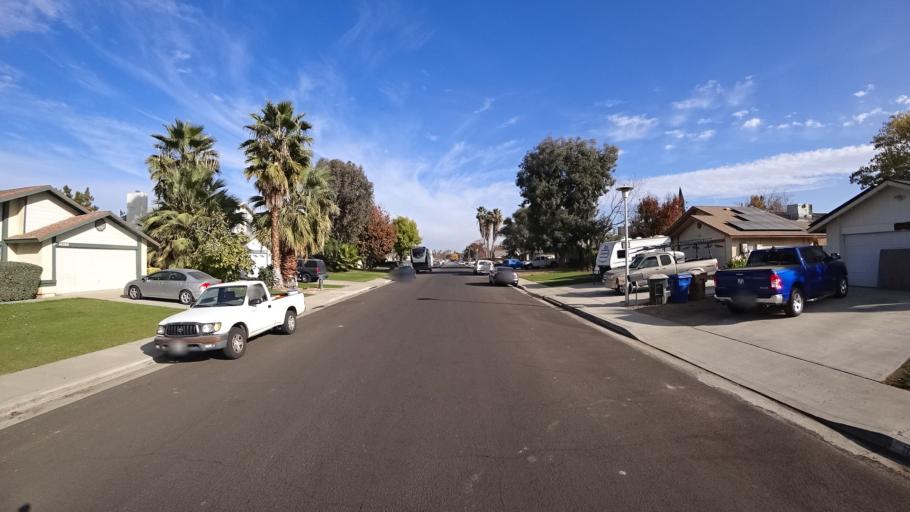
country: US
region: California
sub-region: Kern County
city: Greenacres
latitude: 35.3968
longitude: -119.1156
